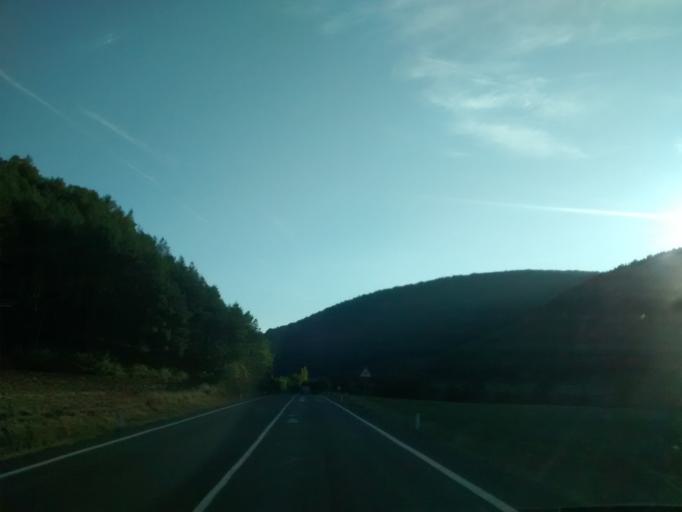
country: ES
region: Aragon
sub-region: Provincia de Huesca
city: Santa Cruz de la Seros
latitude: 42.6085
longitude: -0.7271
